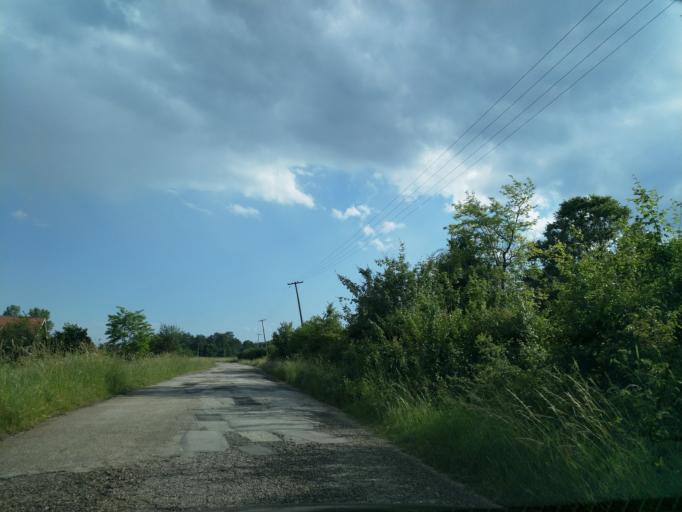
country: RS
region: Central Serbia
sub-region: Borski Okrug
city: Bor
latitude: 43.9888
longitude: 21.9745
